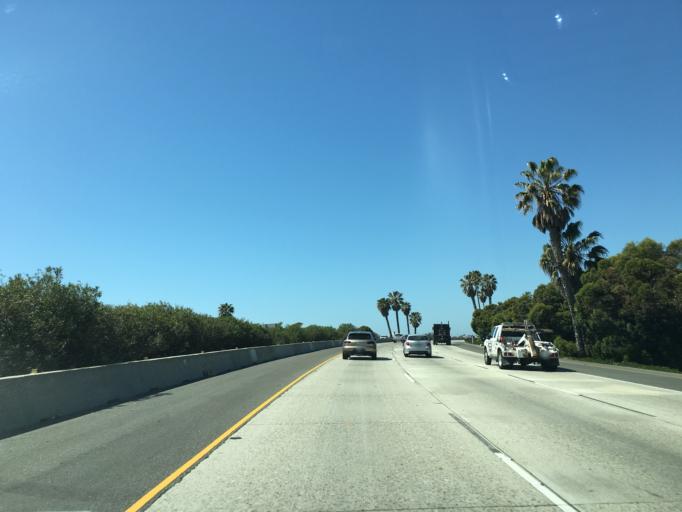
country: US
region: California
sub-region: Ventura County
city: Ventura
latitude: 34.2721
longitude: -119.2809
